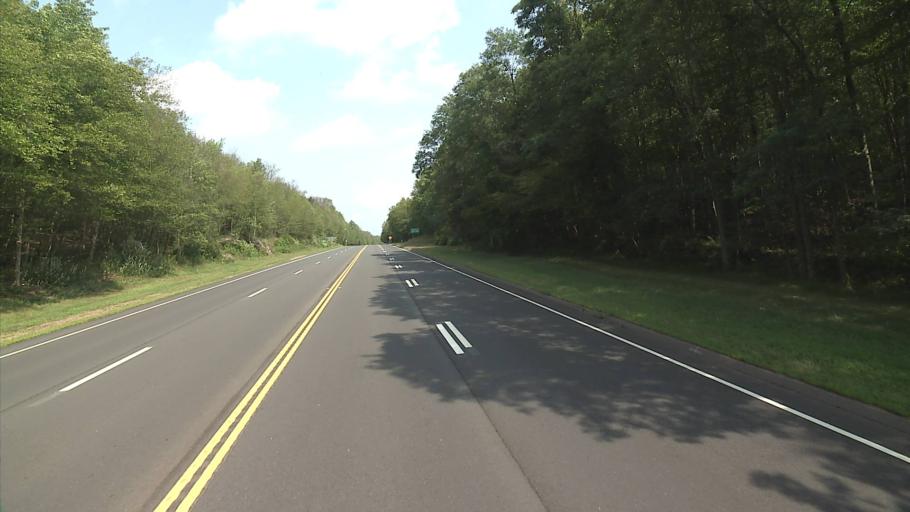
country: US
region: Connecticut
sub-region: Middlesex County
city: East Haddam
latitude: 41.4270
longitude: -72.4905
